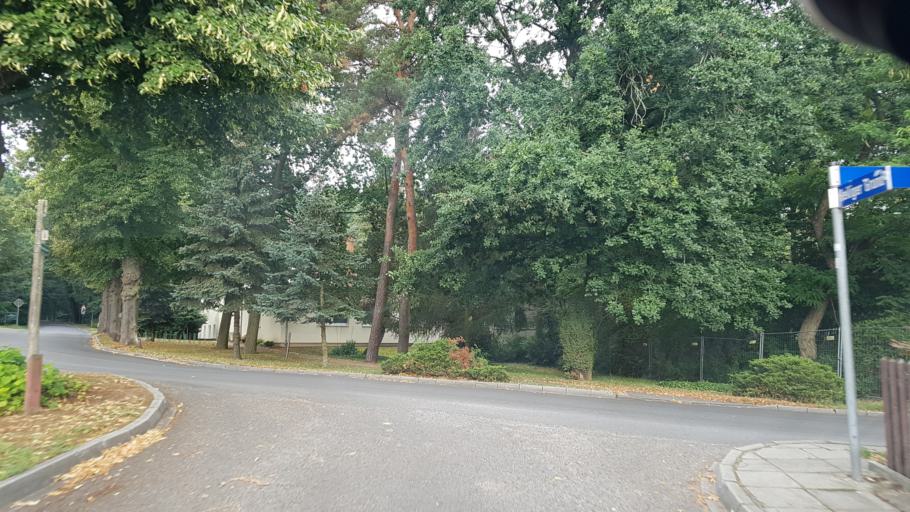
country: DE
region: Brandenburg
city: Hirschfeld
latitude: 51.3813
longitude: 13.6144
